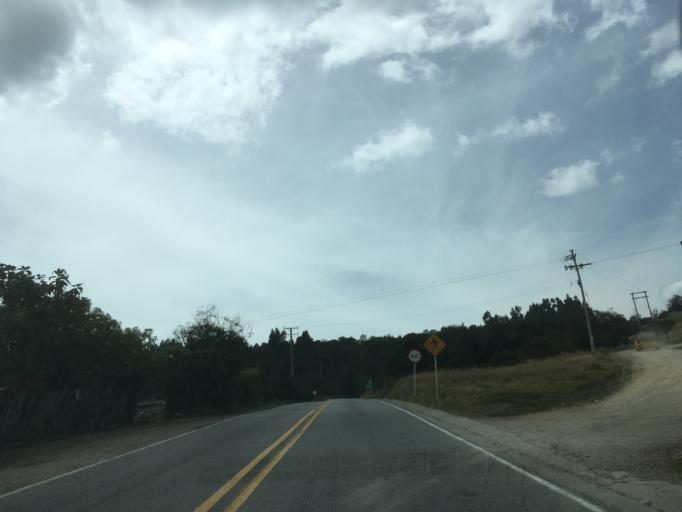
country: CO
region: Boyaca
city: Firavitoba
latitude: 5.6350
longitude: -72.9199
